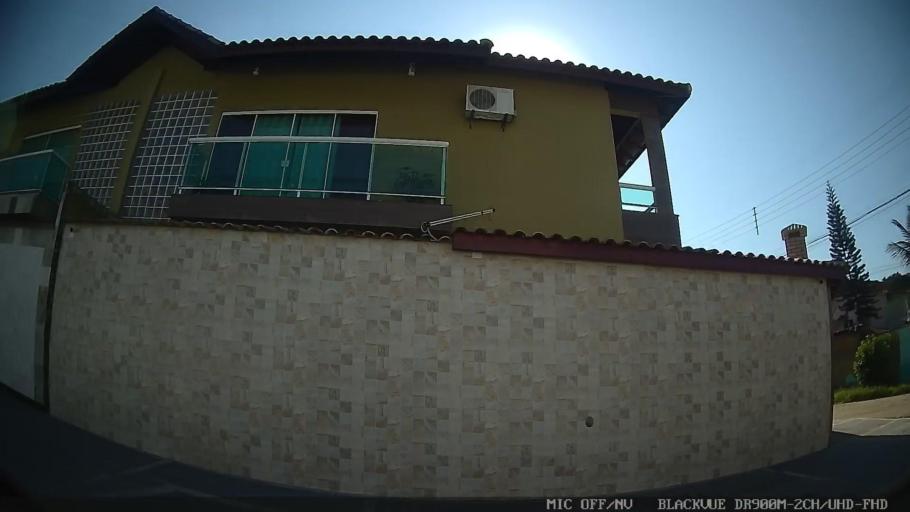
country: BR
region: Sao Paulo
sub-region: Guaruja
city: Guaruja
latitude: -24.0037
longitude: -46.2751
